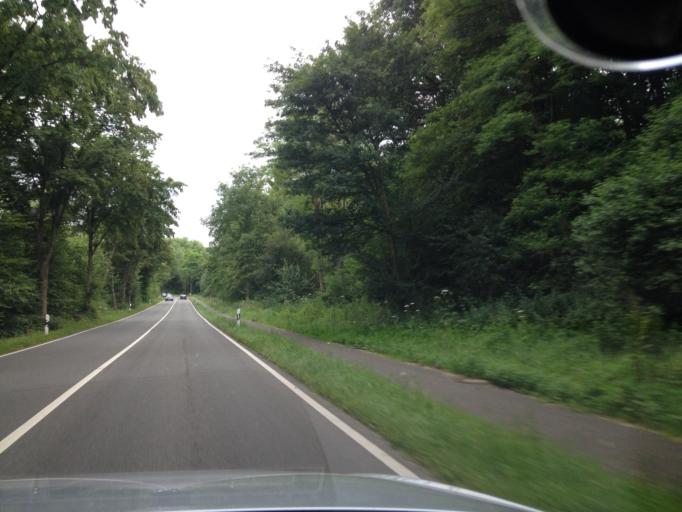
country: DE
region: Saarland
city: Friedrichsthal
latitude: 49.3633
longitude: 7.0928
